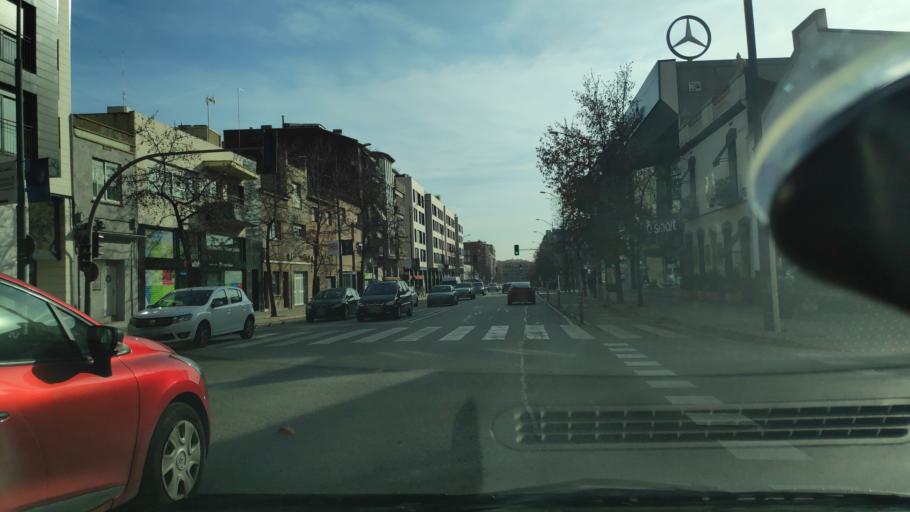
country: ES
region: Catalonia
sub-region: Provincia de Barcelona
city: Sabadell
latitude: 41.5485
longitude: 2.0987
